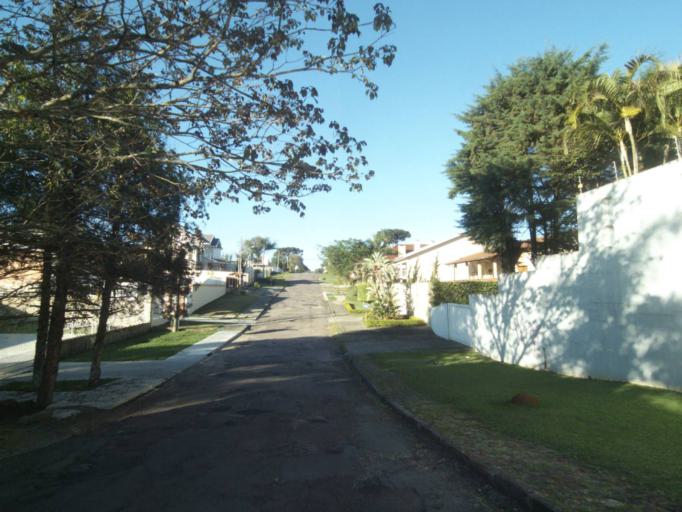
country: BR
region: Parana
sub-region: Curitiba
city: Curitiba
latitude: -25.3947
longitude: -49.2539
